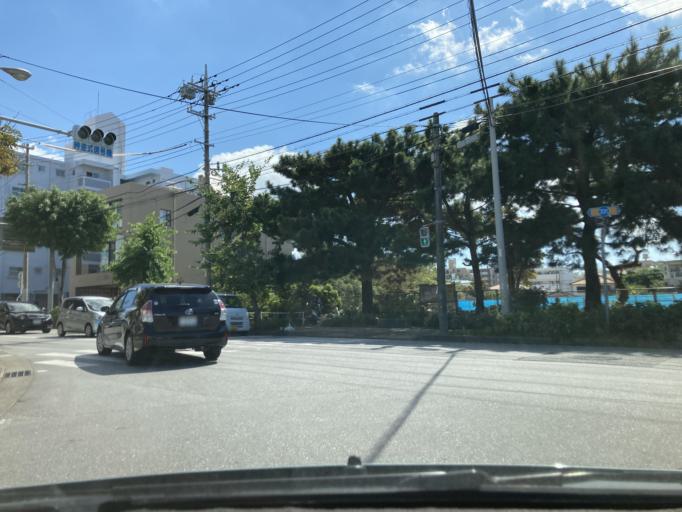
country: JP
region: Okinawa
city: Naha-shi
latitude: 26.2065
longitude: 127.6860
